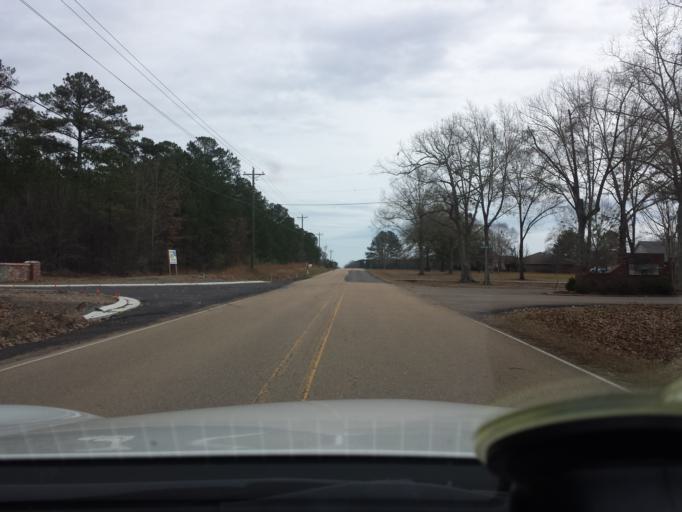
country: US
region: Mississippi
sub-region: Madison County
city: Madison
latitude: 32.4214
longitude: -90.0119
